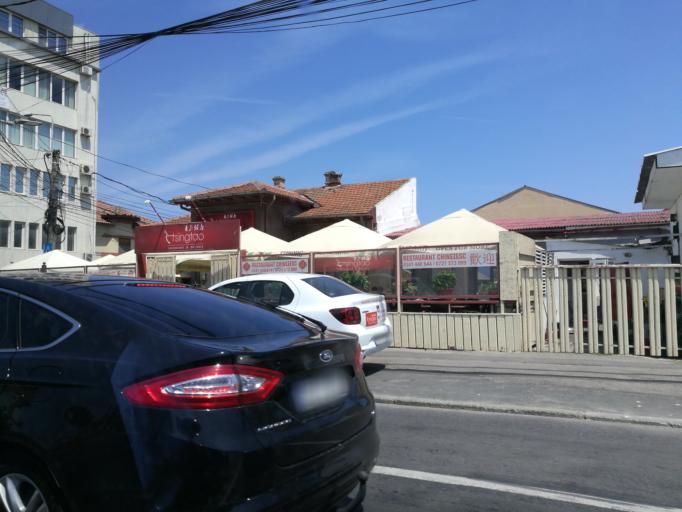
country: RO
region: Constanta
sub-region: Municipiul Constanta
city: Constanta
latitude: 44.1966
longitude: 28.6485
